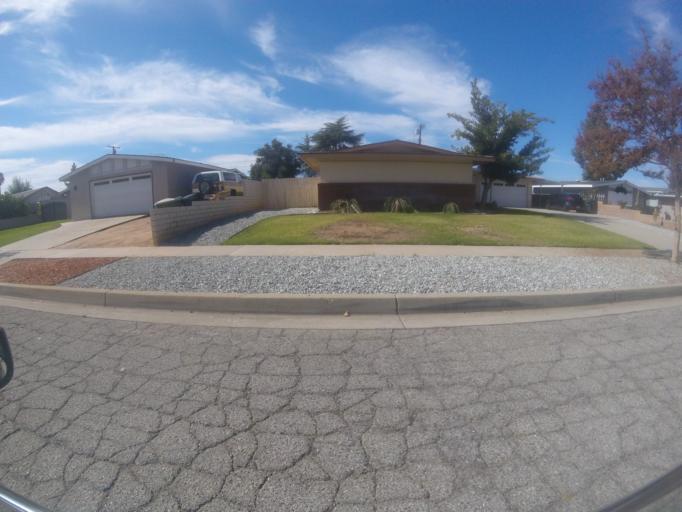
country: US
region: California
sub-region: San Bernardino County
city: Mentone
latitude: 34.0582
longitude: -117.1538
